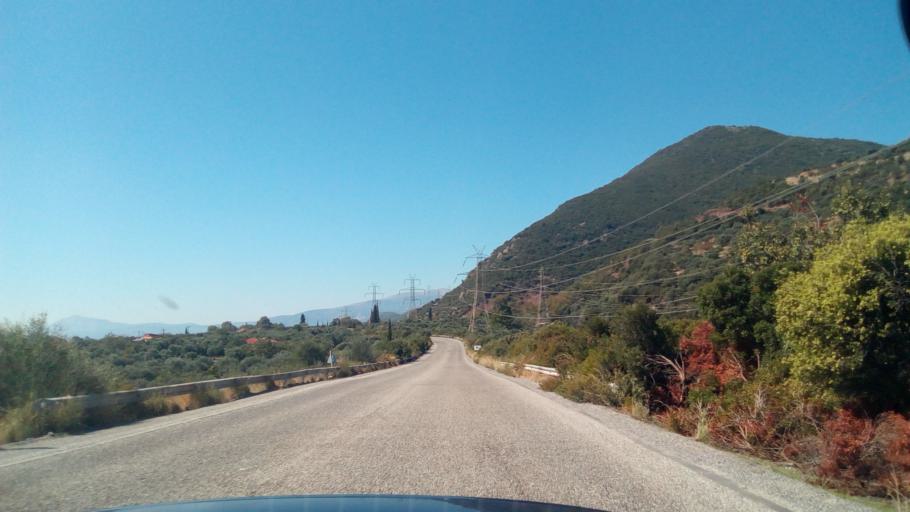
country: GR
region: West Greece
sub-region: Nomos Achaias
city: Kamarai
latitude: 38.3964
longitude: 22.0157
